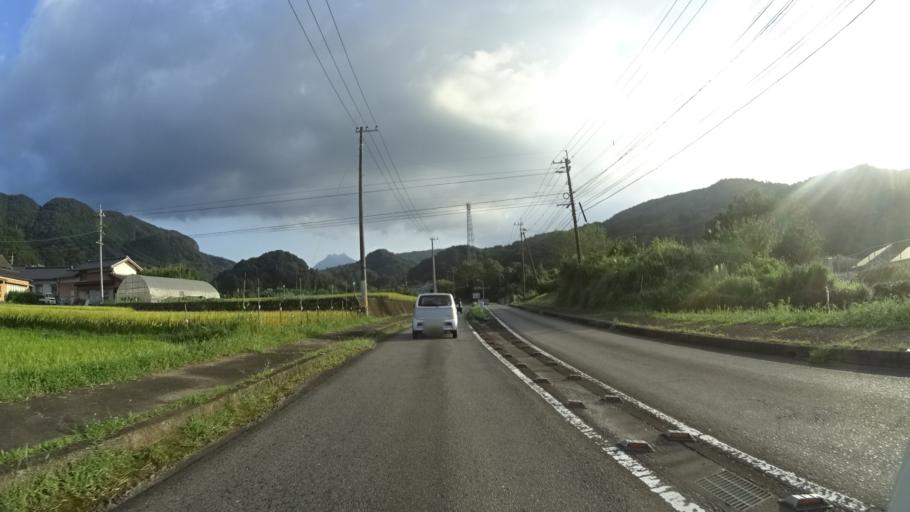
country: JP
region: Oita
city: Hiji
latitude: 33.3763
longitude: 131.3957
